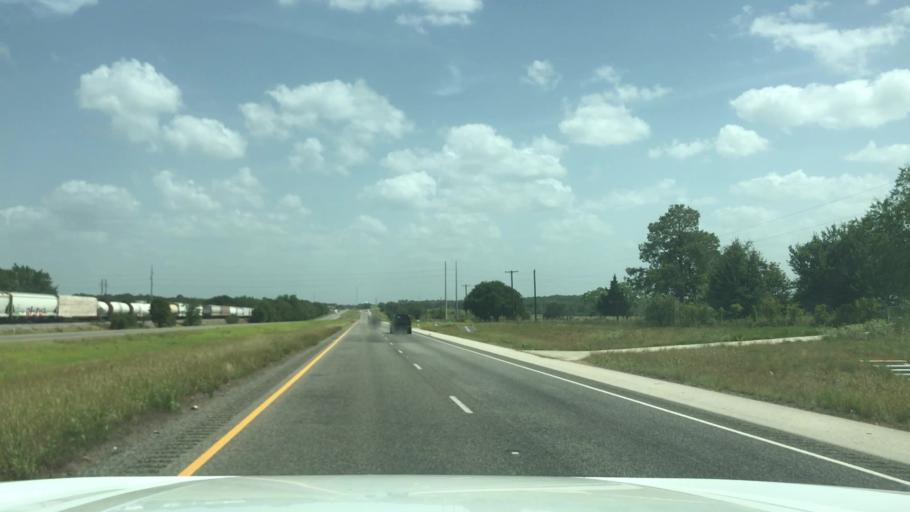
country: US
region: Texas
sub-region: Robertson County
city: Hearne
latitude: 30.9201
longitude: -96.6224
